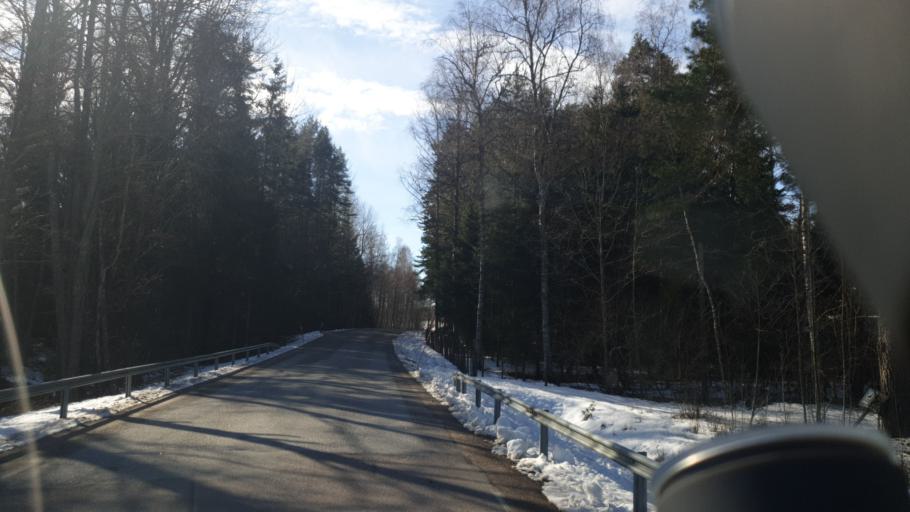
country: SE
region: Vaermland
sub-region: Grums Kommun
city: Slottsbron
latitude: 59.4711
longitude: 12.8797
